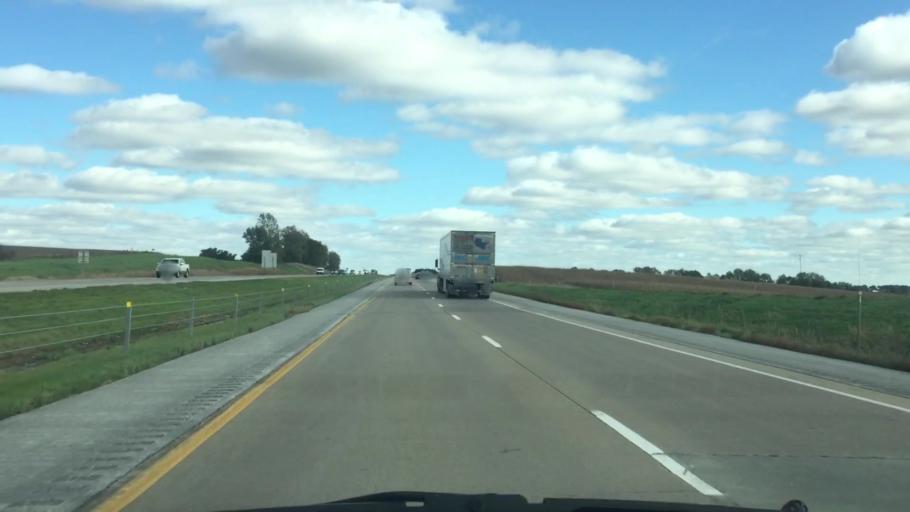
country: US
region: Iowa
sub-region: Muscatine County
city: Wilton
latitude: 41.6357
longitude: -91.0341
